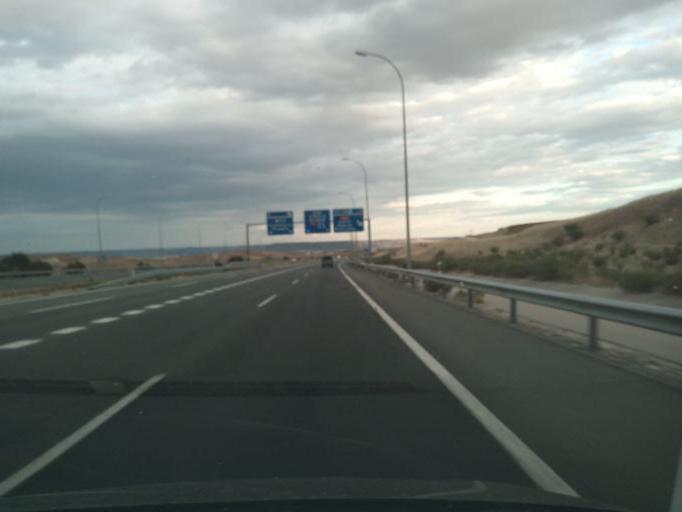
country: ES
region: Madrid
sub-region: Provincia de Madrid
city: Paracuellos de Jarama
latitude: 40.5244
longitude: -3.5109
